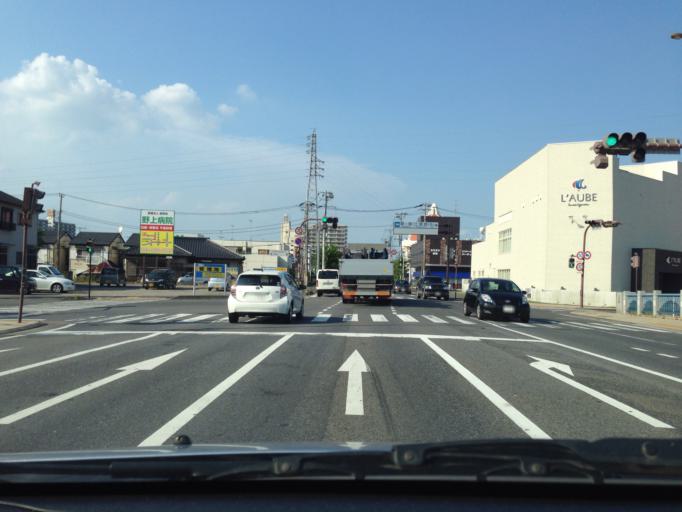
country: JP
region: Ibaraki
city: Ami
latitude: 36.0799
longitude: 140.2089
